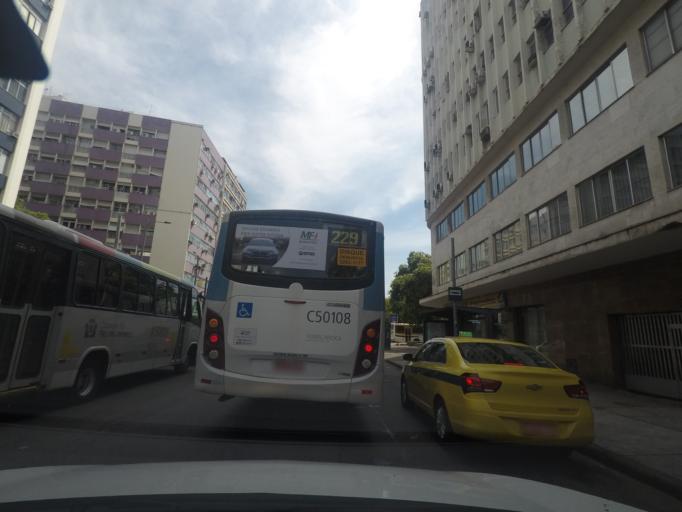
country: BR
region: Rio de Janeiro
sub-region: Rio De Janeiro
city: Rio de Janeiro
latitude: -22.9251
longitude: -43.2338
